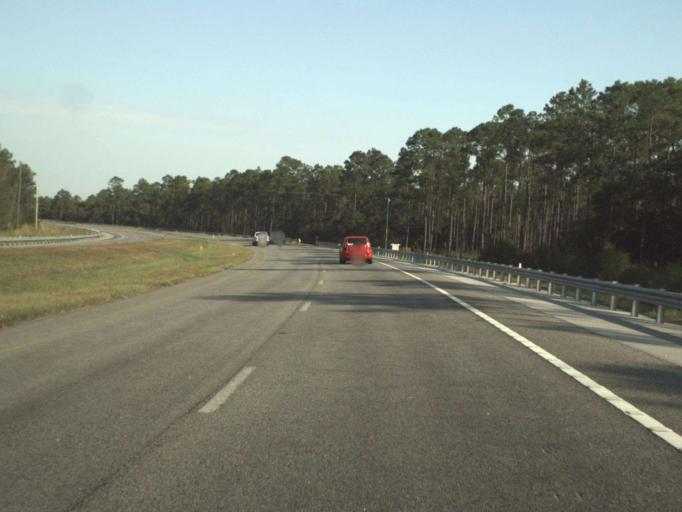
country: US
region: Florida
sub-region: Bay County
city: Laguna Beach
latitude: 30.4146
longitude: -85.8687
